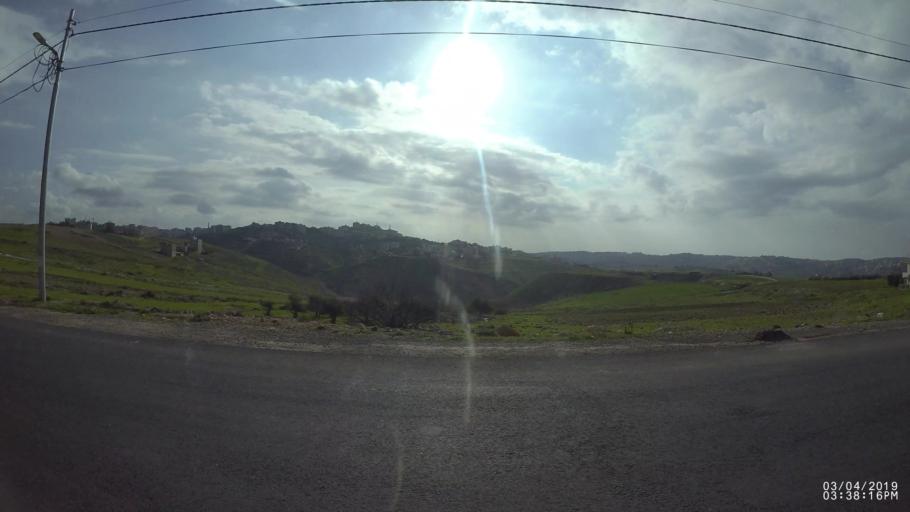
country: JO
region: Amman
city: Umm as Summaq
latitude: 31.9222
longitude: 35.8489
